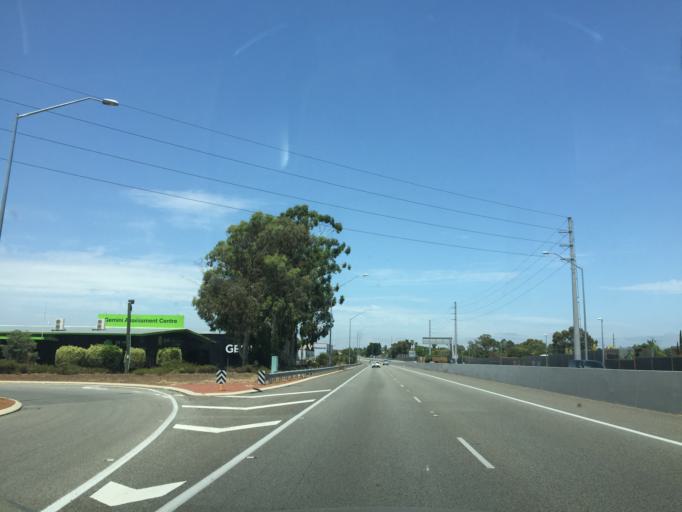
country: AU
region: Western Australia
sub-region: Belmont
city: Kewdale
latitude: -31.9806
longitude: 115.9414
